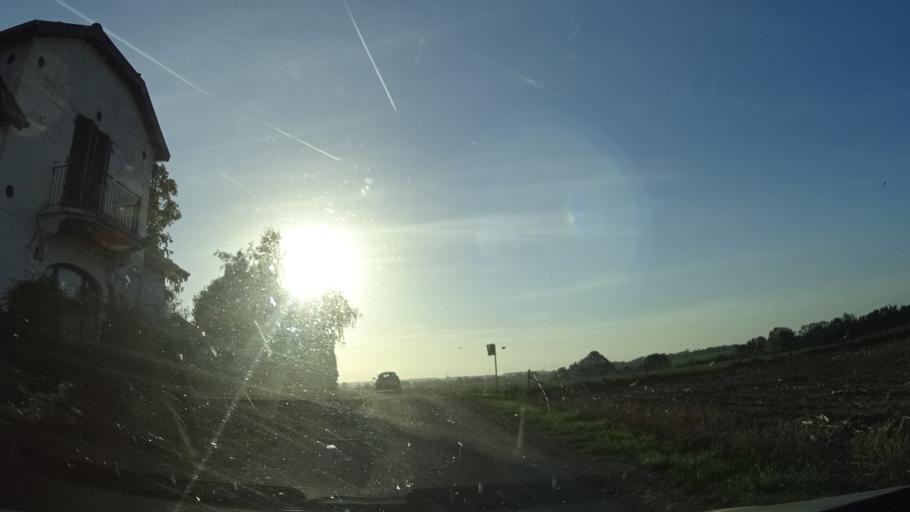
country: BE
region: Wallonia
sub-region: Province du Hainaut
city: Beaumont
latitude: 50.2570
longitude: 4.2458
